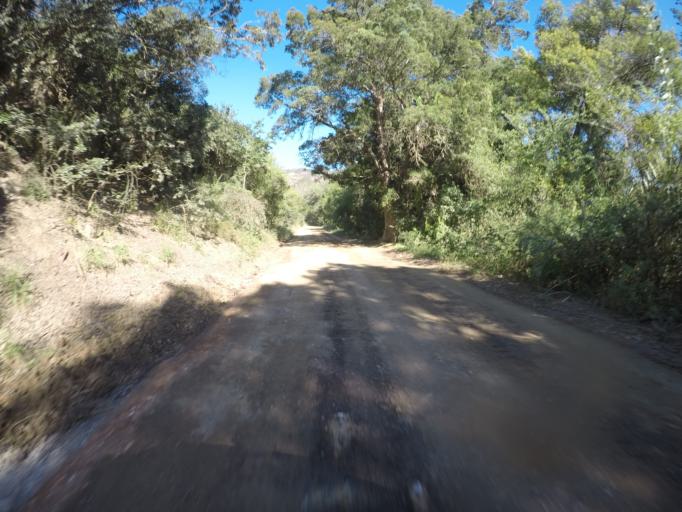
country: ZA
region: Eastern Cape
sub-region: Cacadu District Municipality
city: Kruisfontein
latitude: -33.6634
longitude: 24.5475
